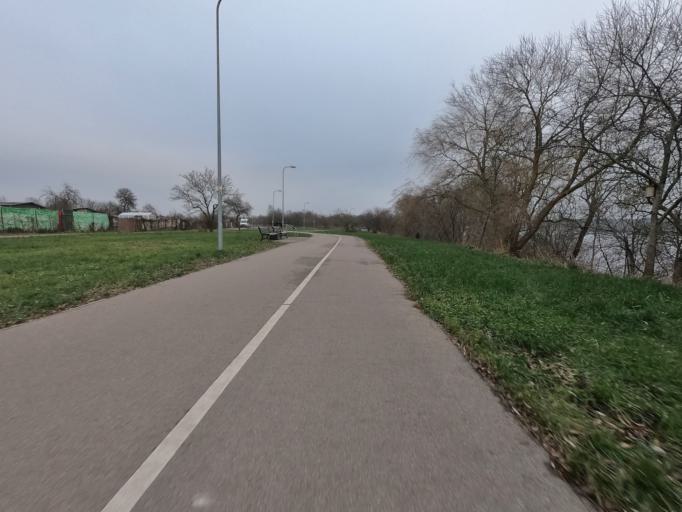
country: LV
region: Kekava
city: Kekava
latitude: 56.8805
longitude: 24.2175
